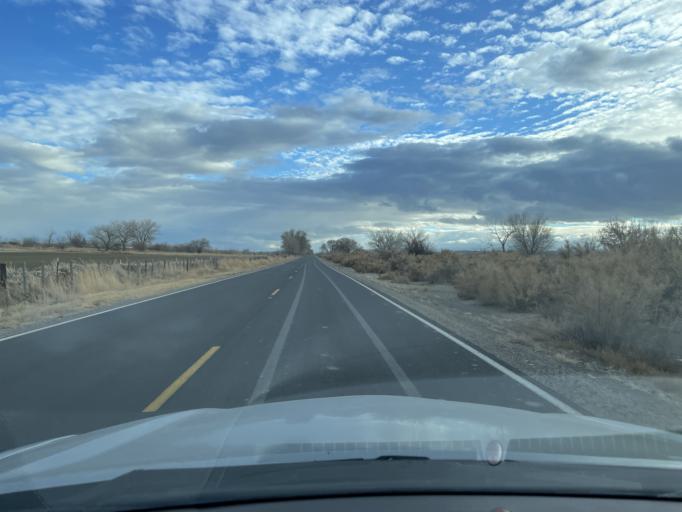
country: US
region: Colorado
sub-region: Montrose County
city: Olathe
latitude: 38.6398
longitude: -107.9923
